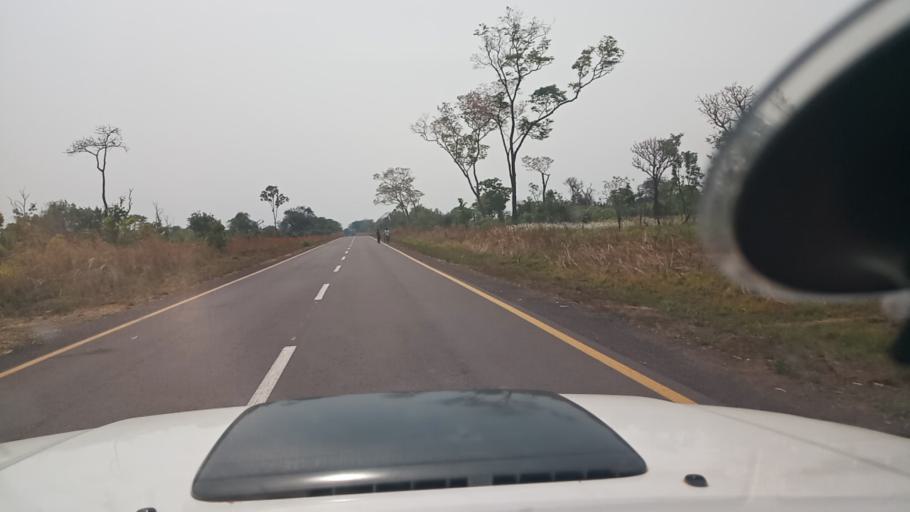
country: ZM
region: Luapula
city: Mansa
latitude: -10.9849
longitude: 28.1279
